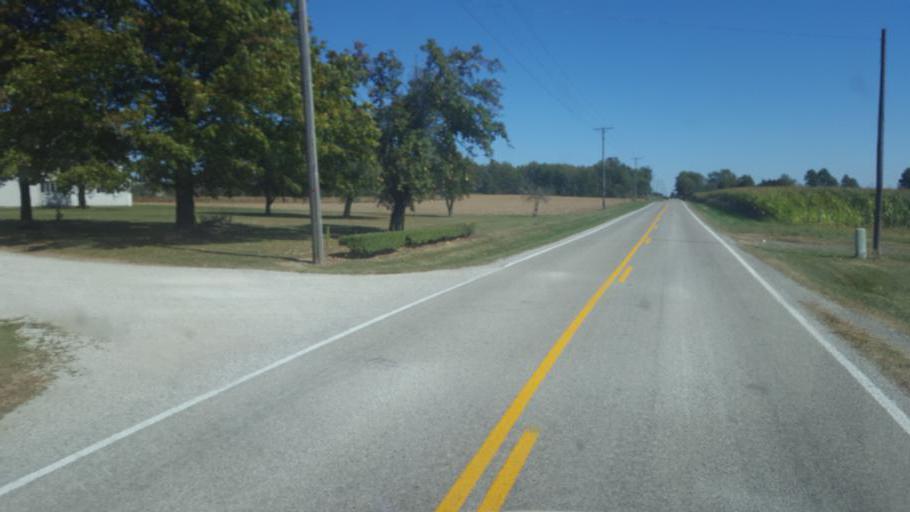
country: US
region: Ohio
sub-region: Huron County
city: Plymouth
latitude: 40.9947
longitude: -82.6348
